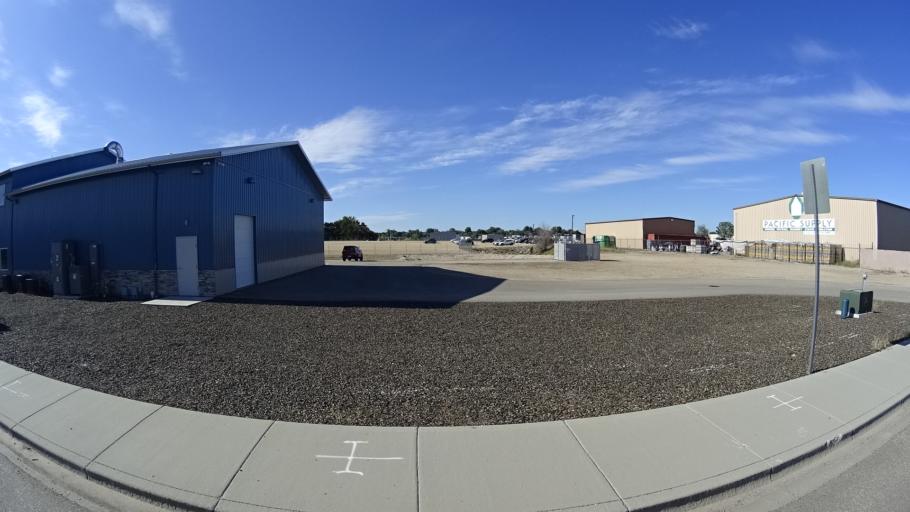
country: US
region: Idaho
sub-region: Ada County
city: Garden City
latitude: 43.5828
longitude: -116.2692
